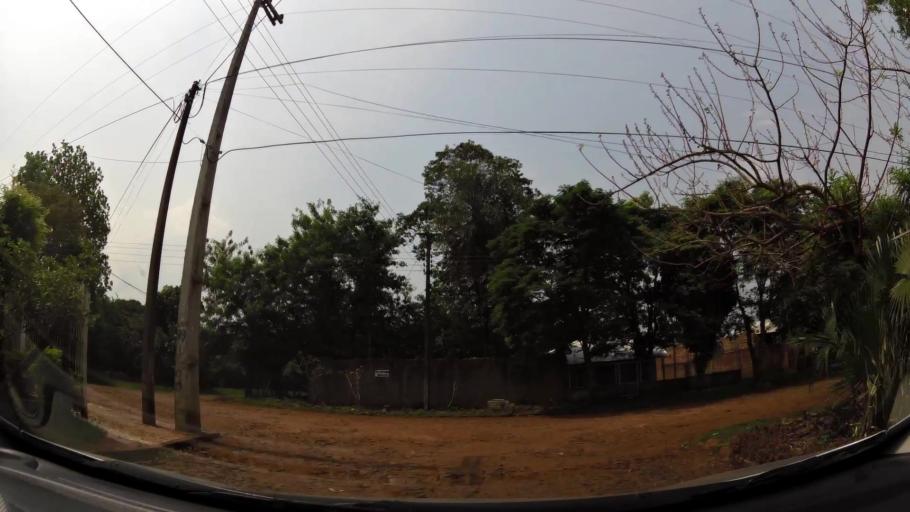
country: PY
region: Alto Parana
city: Presidente Franco
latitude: -25.5576
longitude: -54.6166
